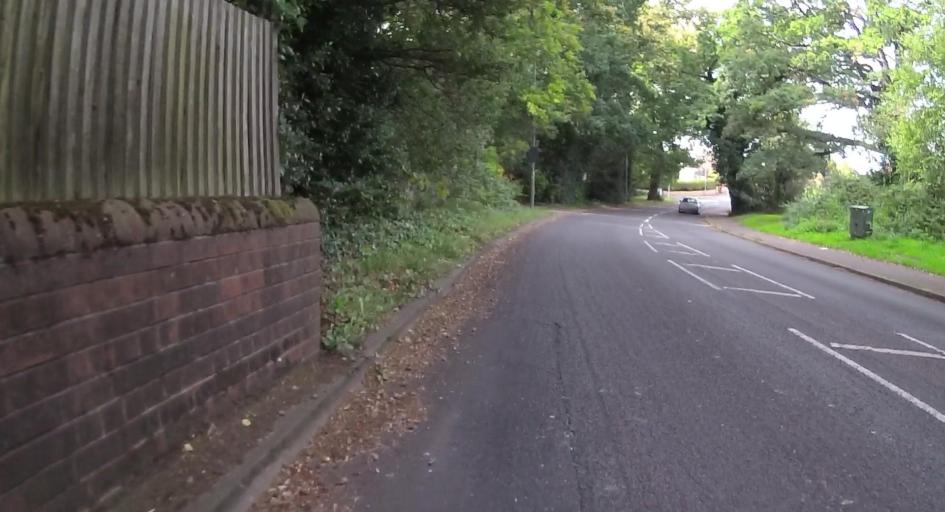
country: GB
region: England
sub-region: Surrey
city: Windlesham
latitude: 51.3484
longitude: -0.6615
